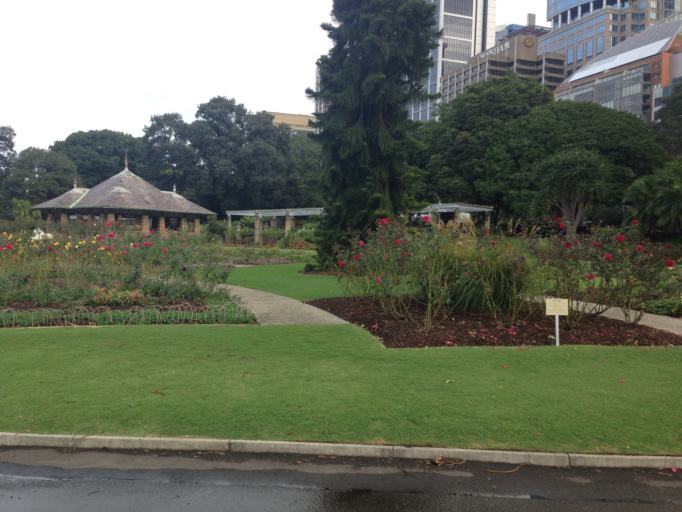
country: AU
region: New South Wales
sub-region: City of Sydney
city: Sydney
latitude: -33.8640
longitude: 151.2141
